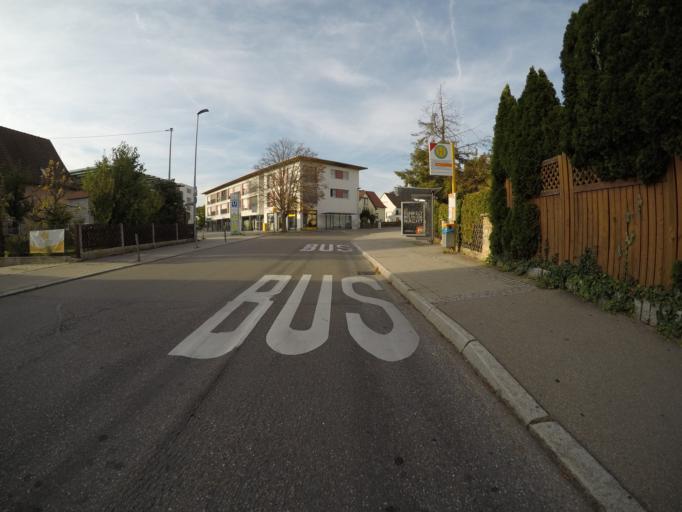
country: DE
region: Baden-Wuerttemberg
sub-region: Regierungsbezirk Stuttgart
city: Esslingen
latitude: 48.7157
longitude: 9.2970
